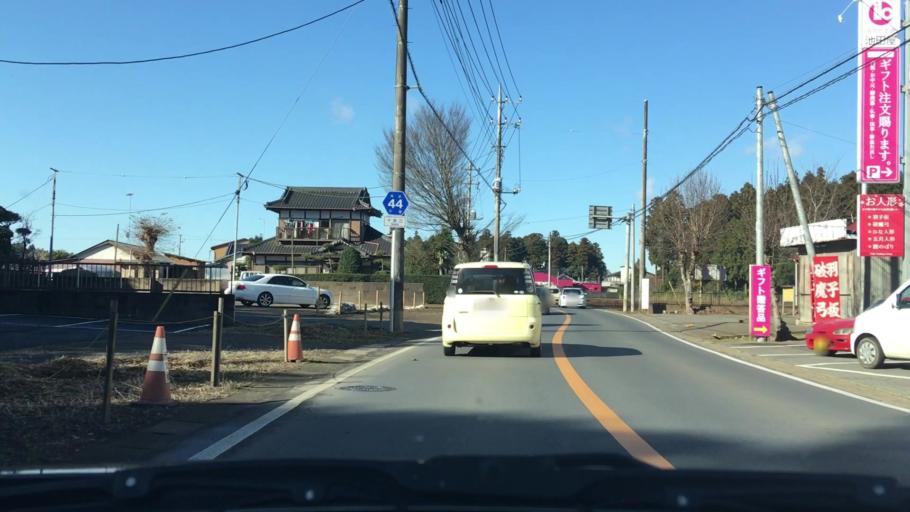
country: JP
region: Chiba
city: Sawara
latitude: 35.7965
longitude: 140.4544
